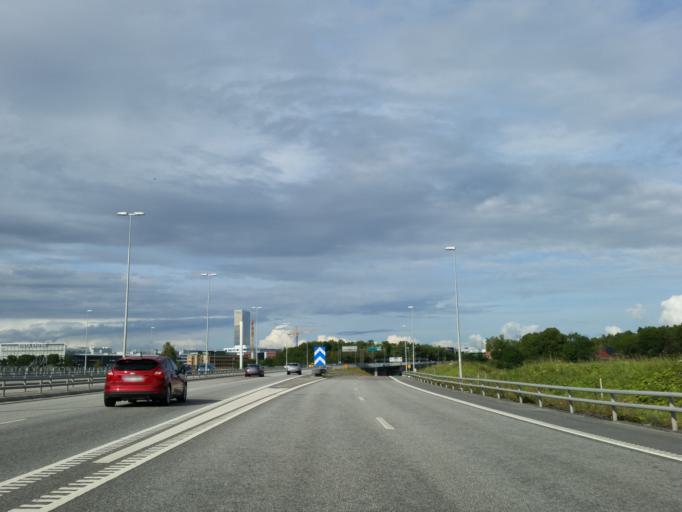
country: SE
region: Stockholm
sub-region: Stockholms Kommun
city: Kista
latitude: 59.3943
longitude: 17.9499
